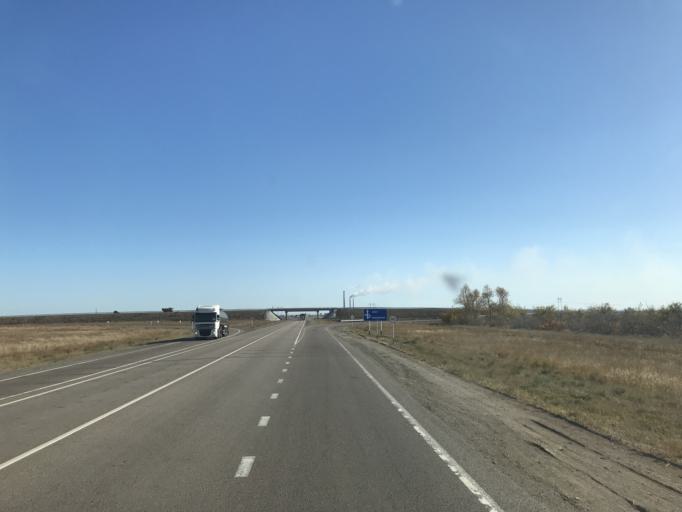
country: KZ
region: Pavlodar
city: Leninskiy
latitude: 52.1561
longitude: 76.8167
